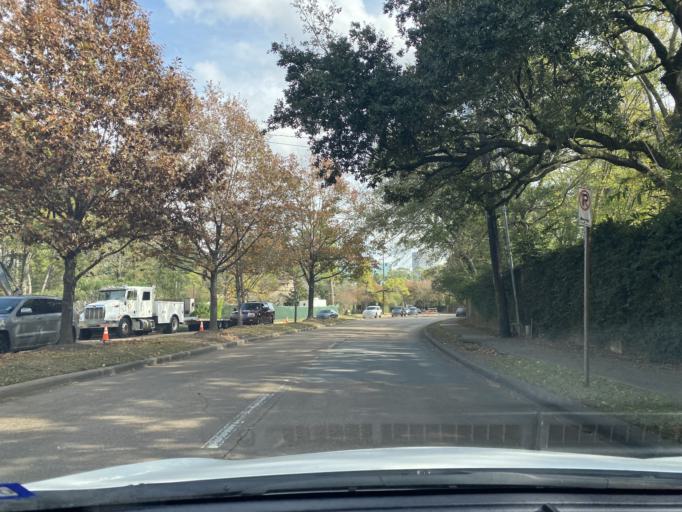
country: US
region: Texas
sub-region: Harris County
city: Hunters Creek Village
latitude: 29.7638
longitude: -95.4722
